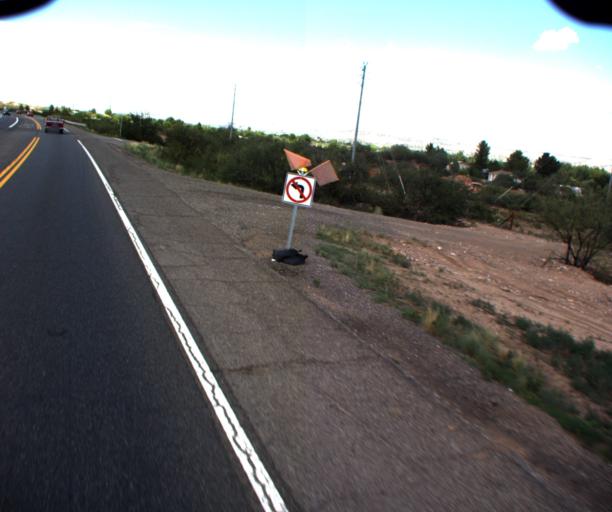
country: US
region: Arizona
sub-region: Yavapai County
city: Camp Verde
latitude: 34.5906
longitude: -111.8885
